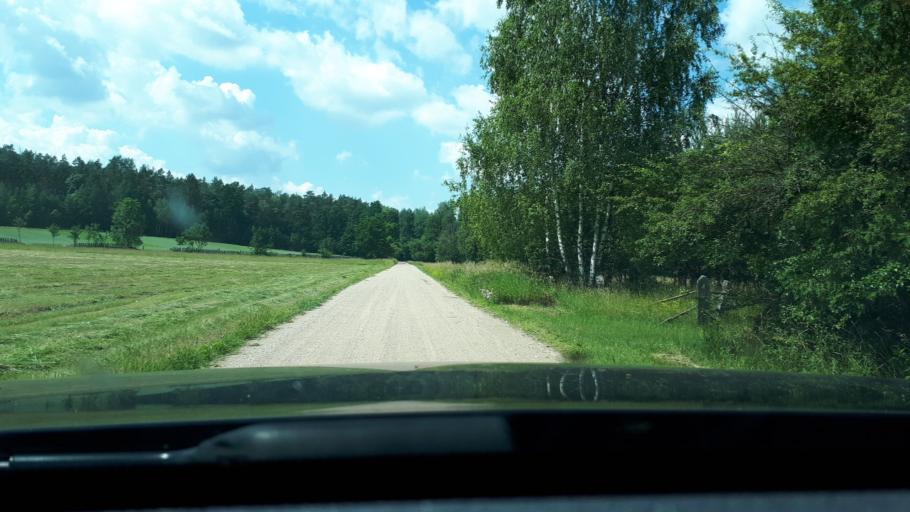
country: PL
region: Podlasie
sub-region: Powiat bialostocki
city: Suprasl
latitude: 53.2420
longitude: 23.3513
